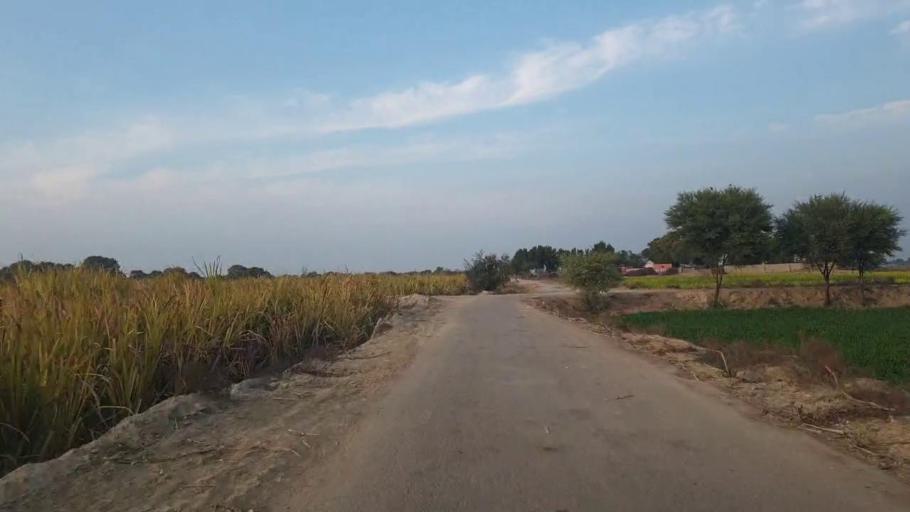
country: PK
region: Sindh
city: Shahpur Chakar
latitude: 26.1090
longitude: 68.5464
